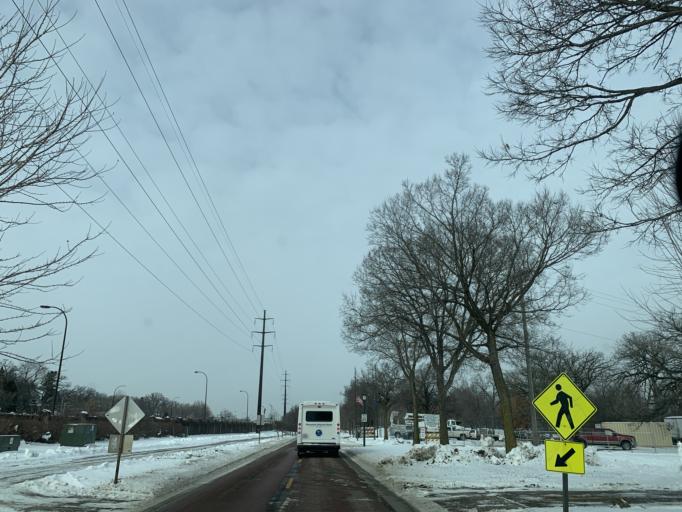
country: US
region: Minnesota
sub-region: Dakota County
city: Mendota Heights
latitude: 44.9111
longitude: -93.2077
